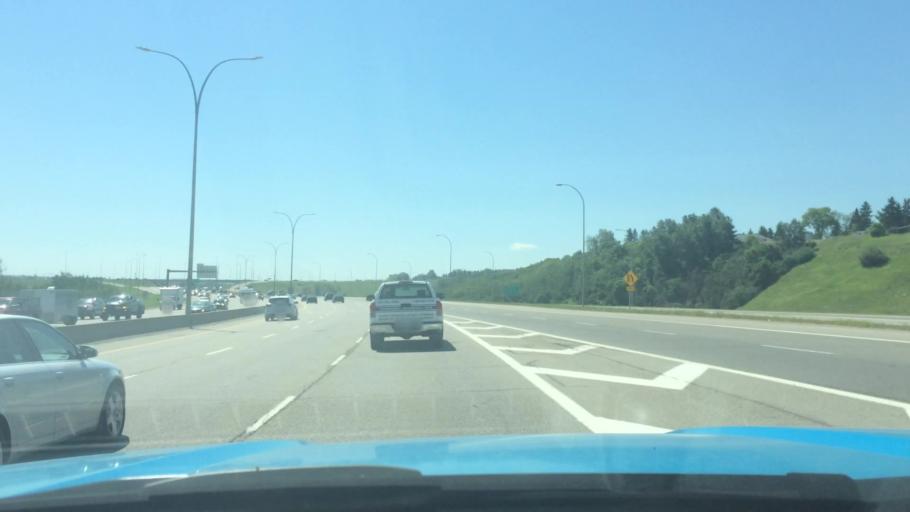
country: CA
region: Alberta
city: Calgary
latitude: 50.9748
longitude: -114.0403
